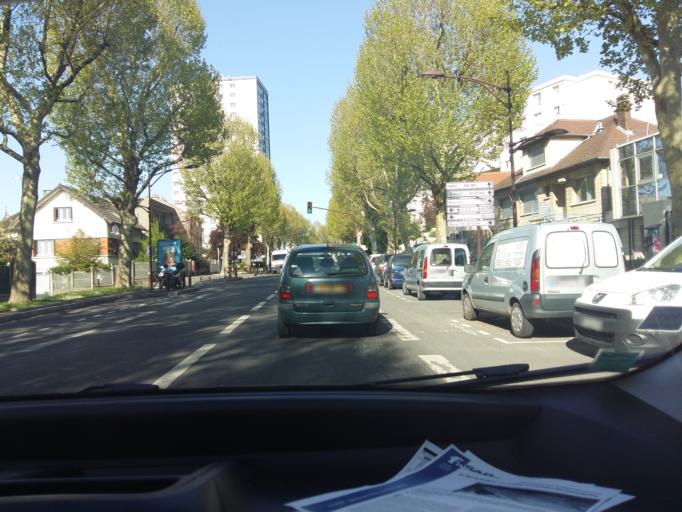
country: FR
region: Ile-de-France
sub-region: Departement du Val-de-Marne
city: Gentilly
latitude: 48.8064
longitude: 2.3506
